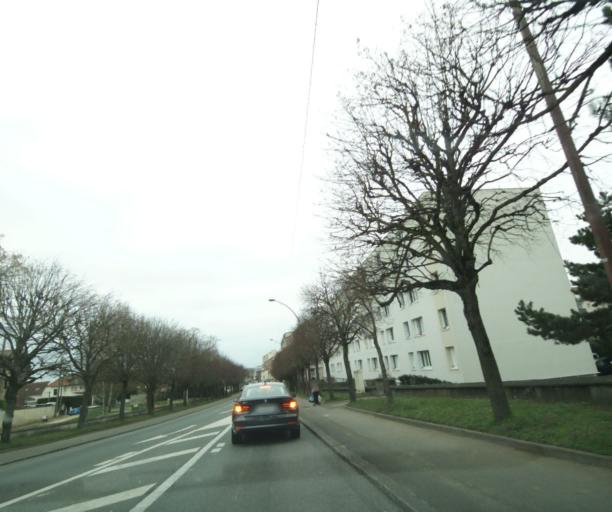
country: FR
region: Ile-de-France
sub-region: Departement des Yvelines
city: Poissy
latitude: 48.9271
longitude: 2.0505
